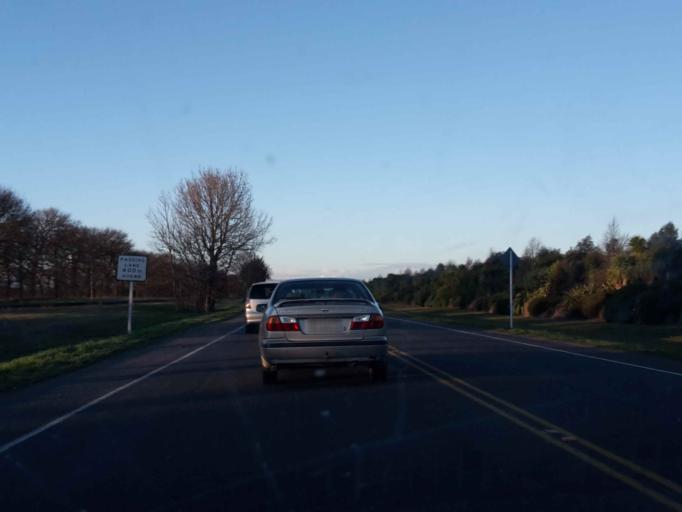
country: NZ
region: Canterbury
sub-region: Selwyn District
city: Rolleston
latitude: -43.5870
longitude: 172.3885
